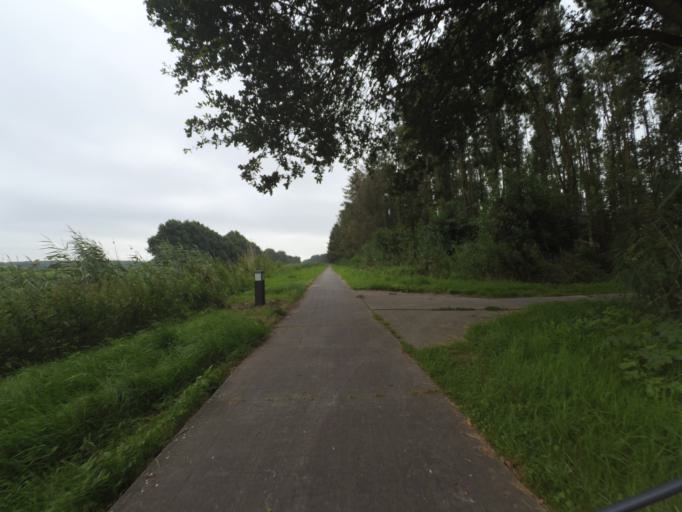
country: NL
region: Flevoland
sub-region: Gemeente Lelystad
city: Lelystad
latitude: 52.4584
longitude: 5.5377
